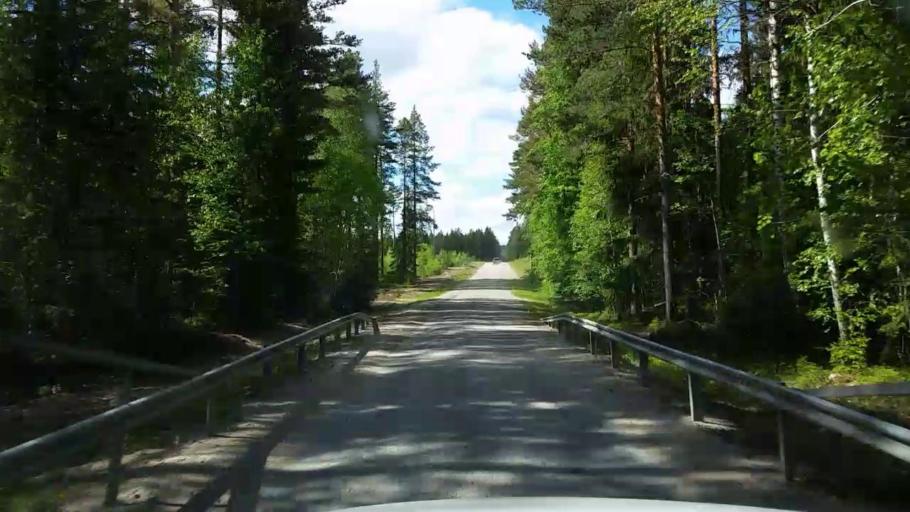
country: SE
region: Gaevleborg
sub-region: Ovanakers Kommun
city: Edsbyn
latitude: 61.5724
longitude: 15.9183
